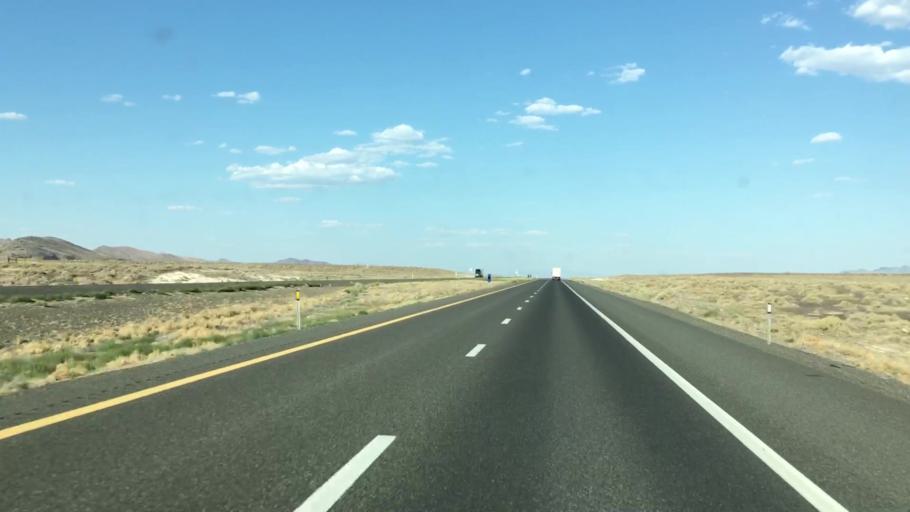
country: US
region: Nevada
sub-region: Churchill County
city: Fallon
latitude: 39.8573
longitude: -118.9177
